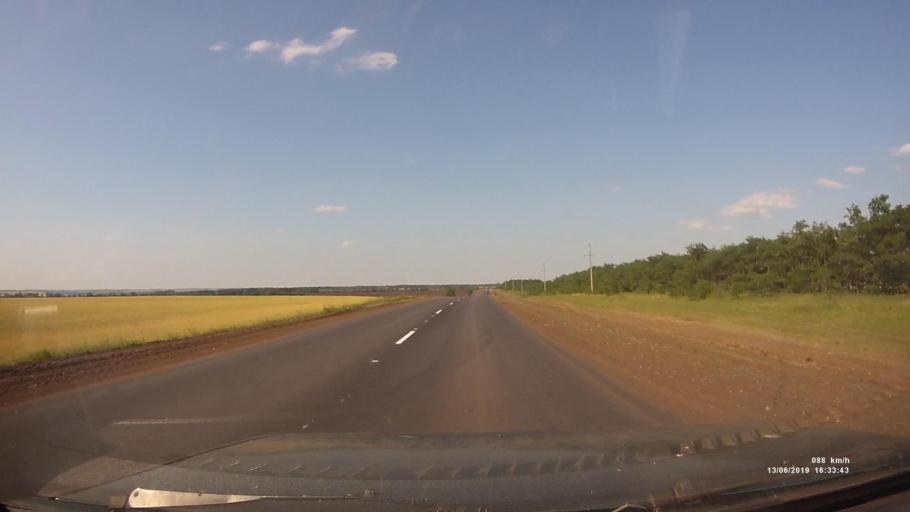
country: RU
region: Rostov
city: Kazanskaya
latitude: 49.8639
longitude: 41.2831
